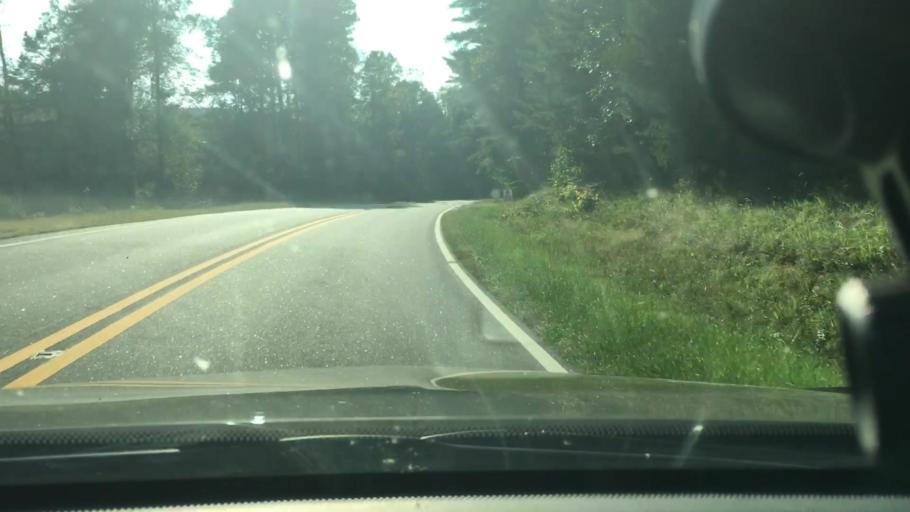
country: US
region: North Carolina
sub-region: Rutherford County
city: Rutherfordton
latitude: 35.3256
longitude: -82.0755
